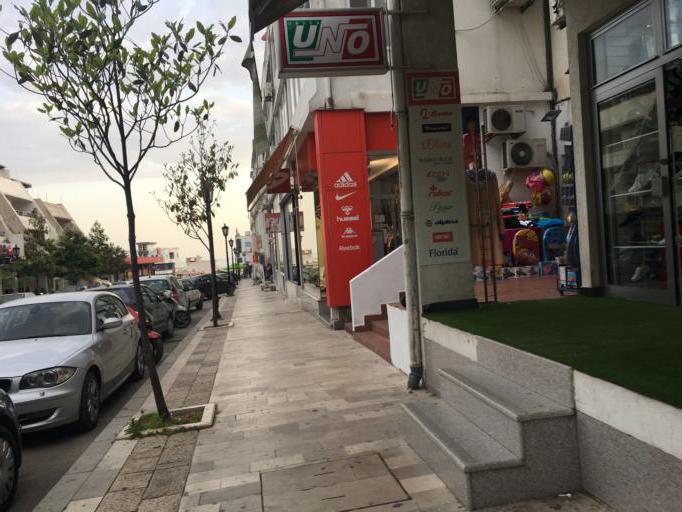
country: ME
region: Ulcinj
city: Ulcinj
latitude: 41.9283
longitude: 19.2064
